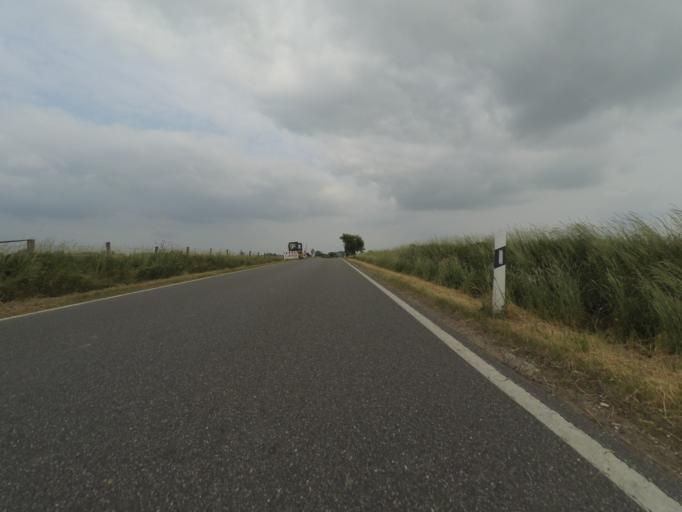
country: DE
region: Mecklenburg-Vorpommern
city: Lubz
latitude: 53.4075
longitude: 12.1121
